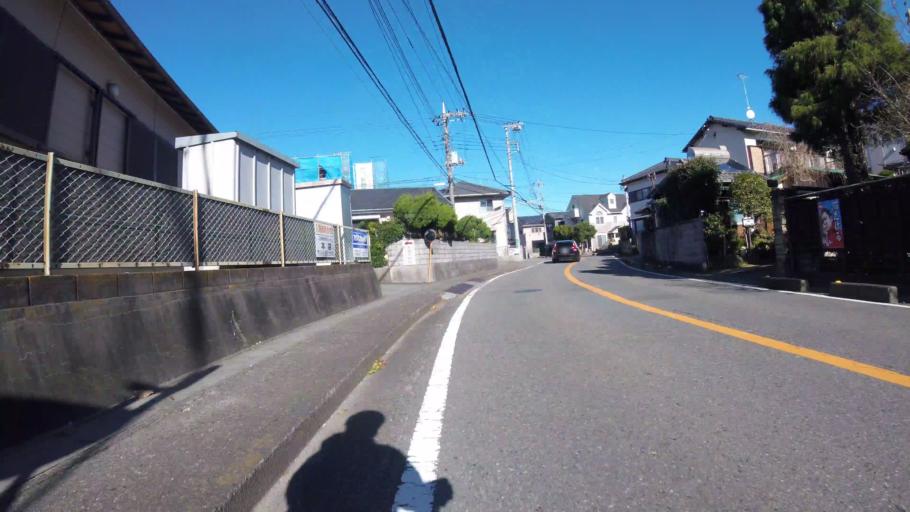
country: JP
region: Shizuoka
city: Mishima
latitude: 35.1317
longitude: 138.9194
